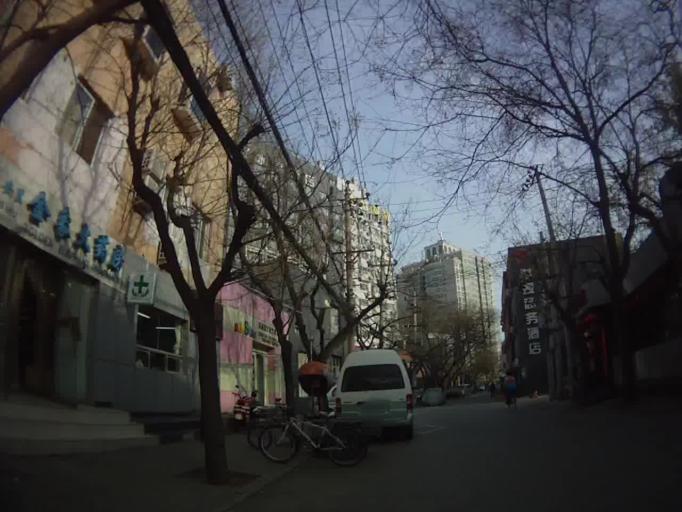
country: CN
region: Beijing
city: Chaowai
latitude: 39.9045
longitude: 116.4410
